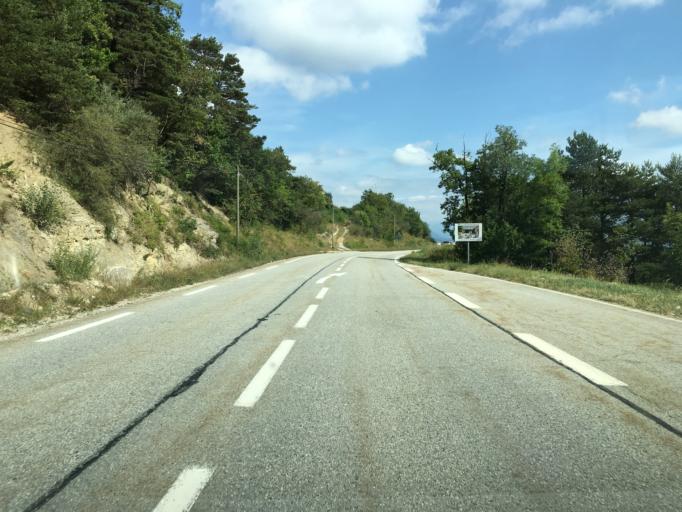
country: FR
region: Rhone-Alpes
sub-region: Departement de l'Isere
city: Mens
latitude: 44.7670
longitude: 5.6611
